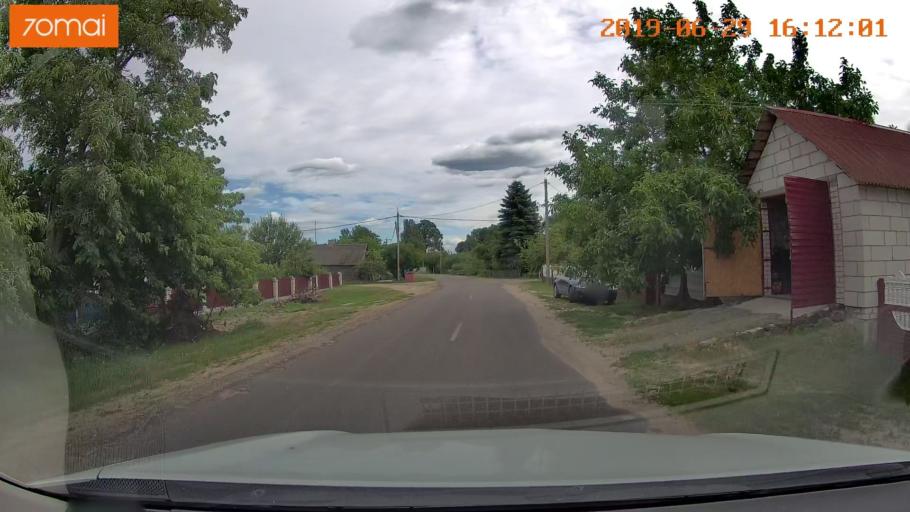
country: BY
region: Brest
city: Luninyets
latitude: 52.2023
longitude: 27.0127
